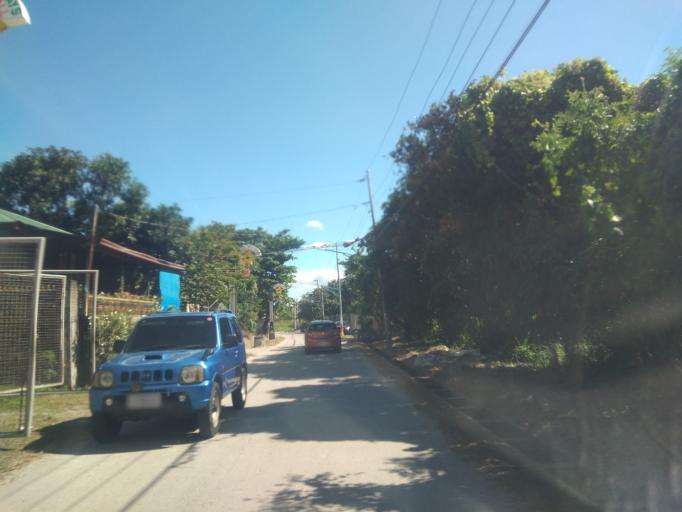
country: PH
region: Central Luzon
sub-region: Province of Pampanga
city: Bacolor
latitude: 14.9977
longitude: 120.6501
